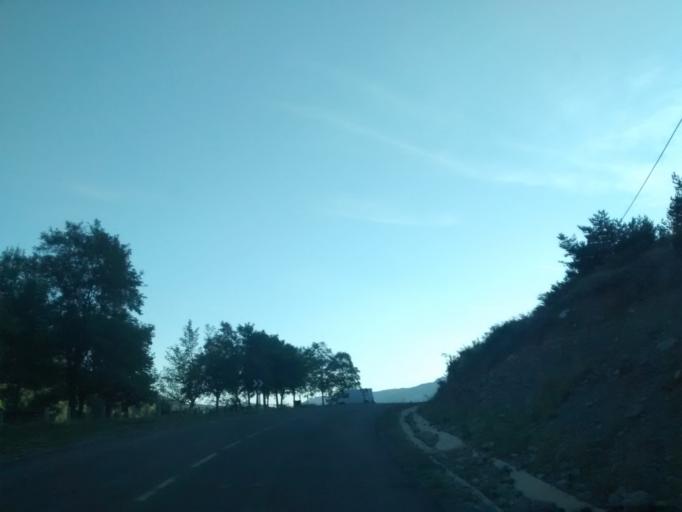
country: ES
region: Aragon
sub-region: Provincia de Huesca
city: Anso
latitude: 42.7658
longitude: -0.7448
